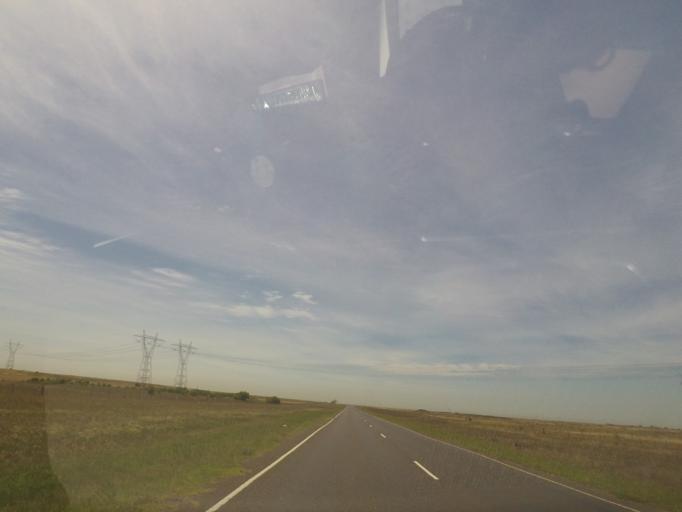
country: AU
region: Victoria
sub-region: Wyndham
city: Wyndham Vale
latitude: -37.8170
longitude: 144.5213
